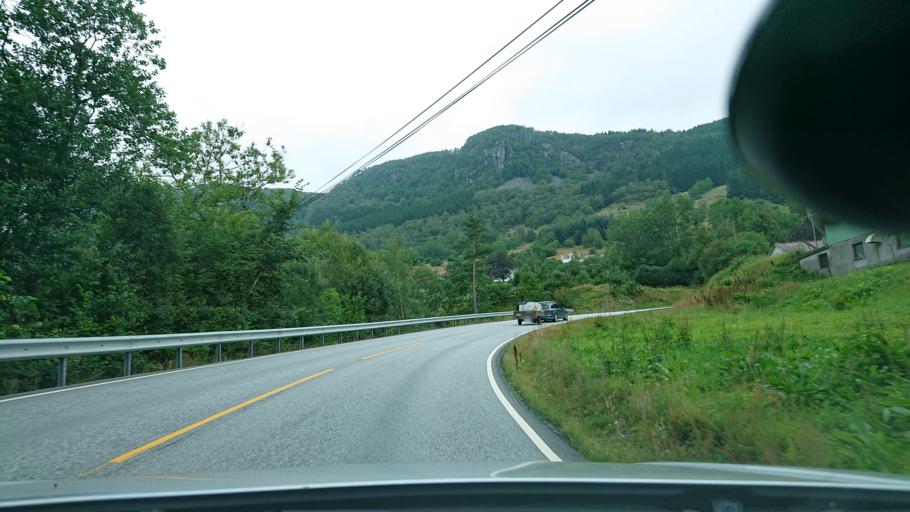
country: NO
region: Rogaland
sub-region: Hjelmeland
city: Hjelmelandsvagen
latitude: 59.1668
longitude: 6.1675
